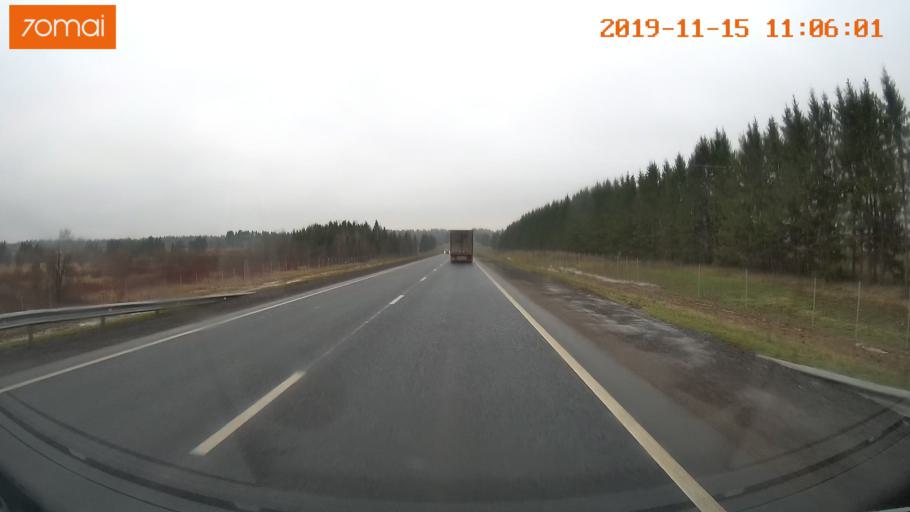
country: RU
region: Vologda
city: Chebsara
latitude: 59.1187
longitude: 39.0170
